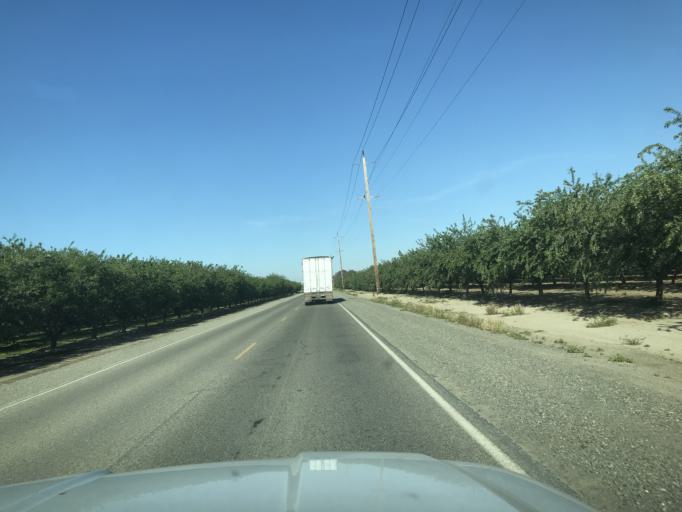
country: US
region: California
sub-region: Fresno County
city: Kerman
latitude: 36.6618
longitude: -120.1202
